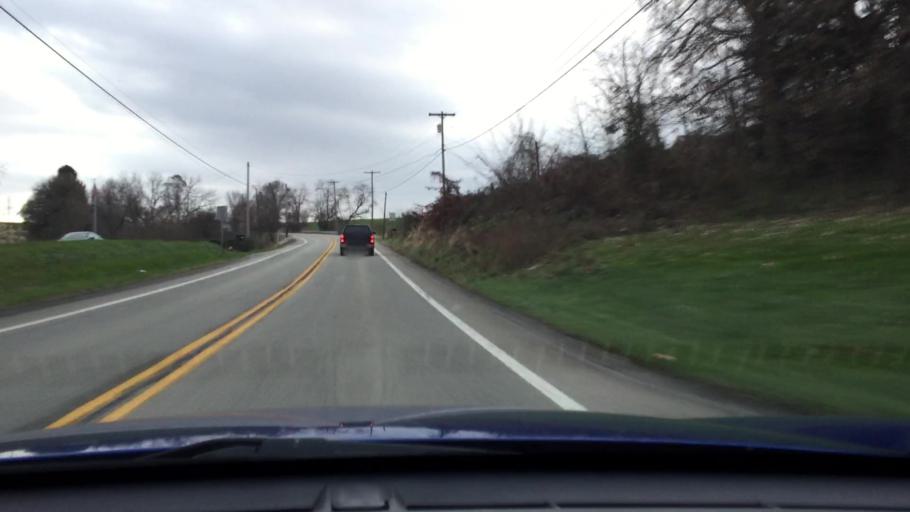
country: US
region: Pennsylvania
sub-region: Allegheny County
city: Elizabeth
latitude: 40.2463
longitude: -79.8588
